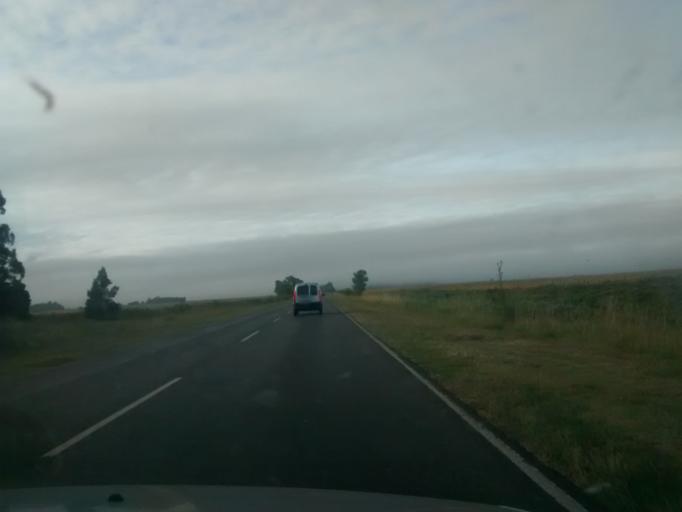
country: AR
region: Buenos Aires
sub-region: Partido de Brandsen
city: Brandsen
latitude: -35.3366
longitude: -58.2446
